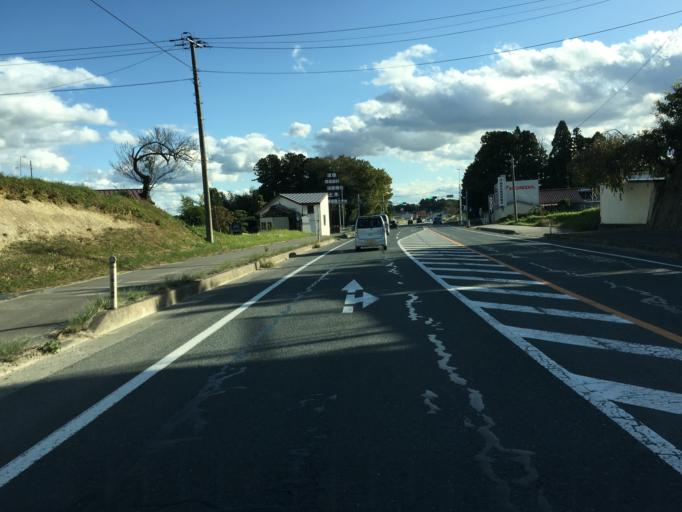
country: JP
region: Miyagi
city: Marumori
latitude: 37.8740
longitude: 140.9191
